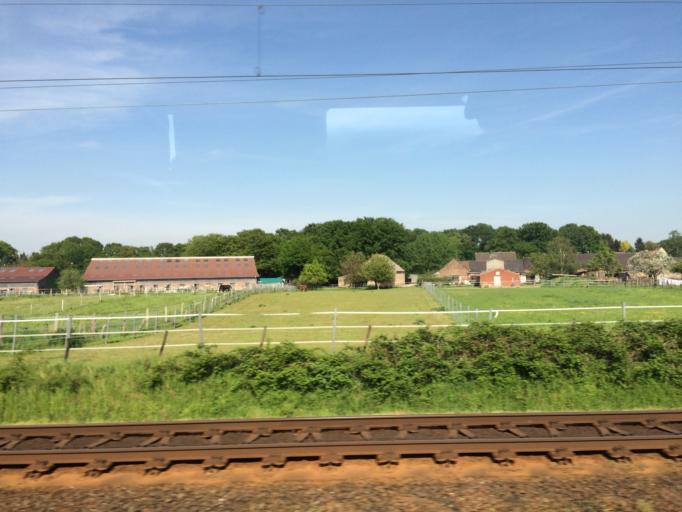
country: DE
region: North Rhine-Westphalia
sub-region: Regierungsbezirk Dusseldorf
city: Langenfeld
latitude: 51.0791
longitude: 6.9526
